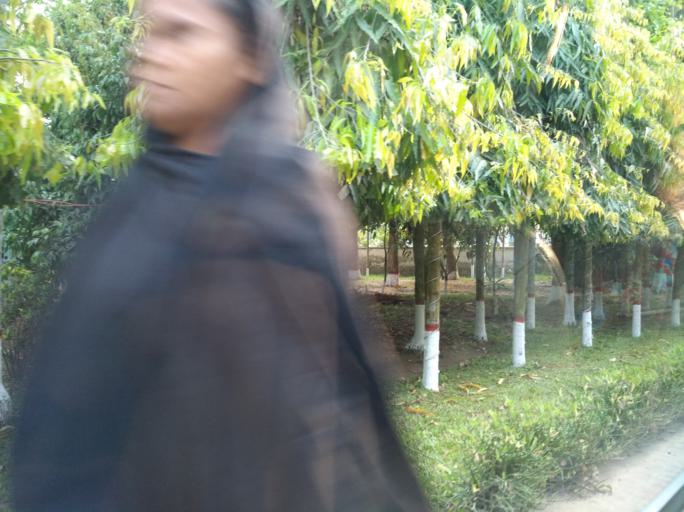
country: BD
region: Rajshahi
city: Bogra
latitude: 24.7050
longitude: 89.3969
